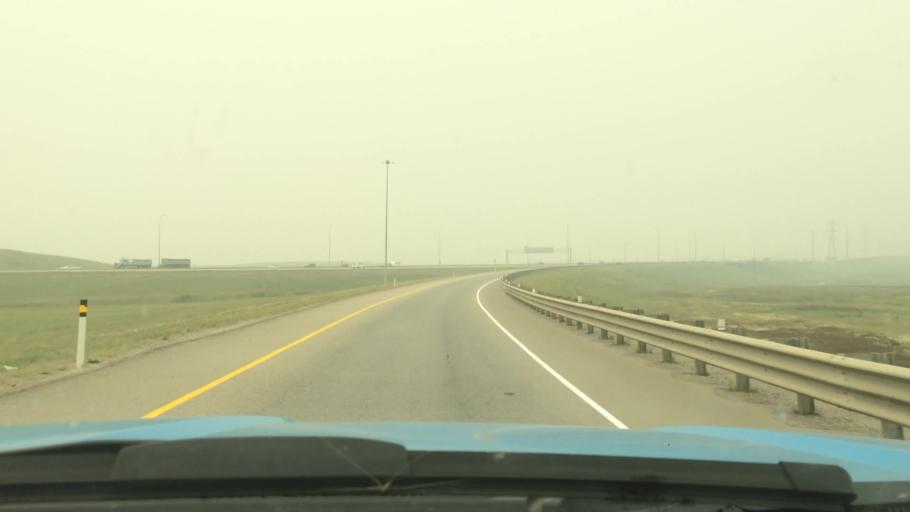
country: CA
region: Alberta
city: Airdrie
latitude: 51.1774
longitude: -114.0078
